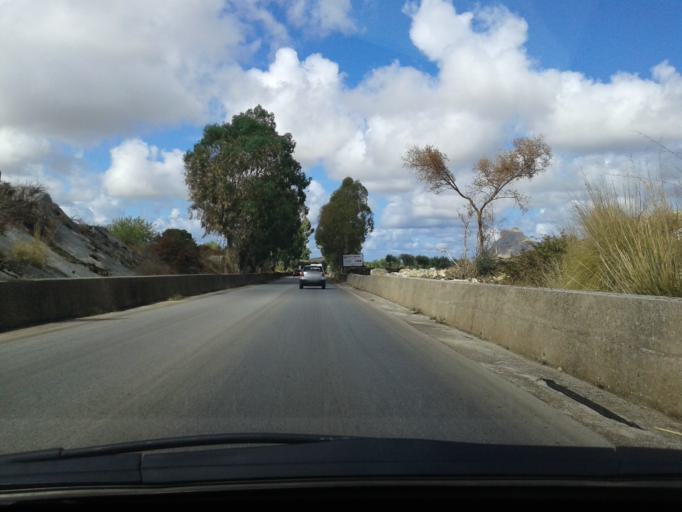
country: IT
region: Sicily
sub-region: Trapani
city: Castelluzzo
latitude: 38.0750
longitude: 12.7389
